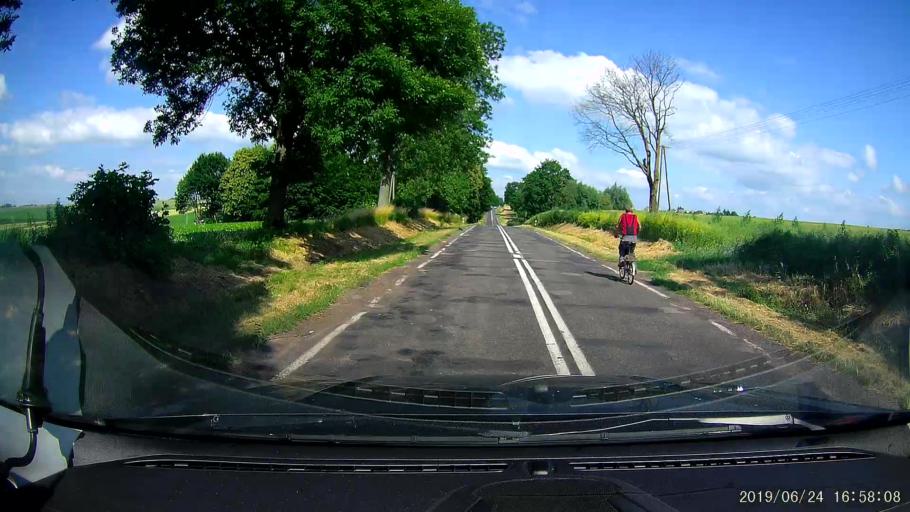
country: PL
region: Lublin Voivodeship
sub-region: Powiat tomaszowski
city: Telatyn
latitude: 50.5256
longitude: 23.8735
